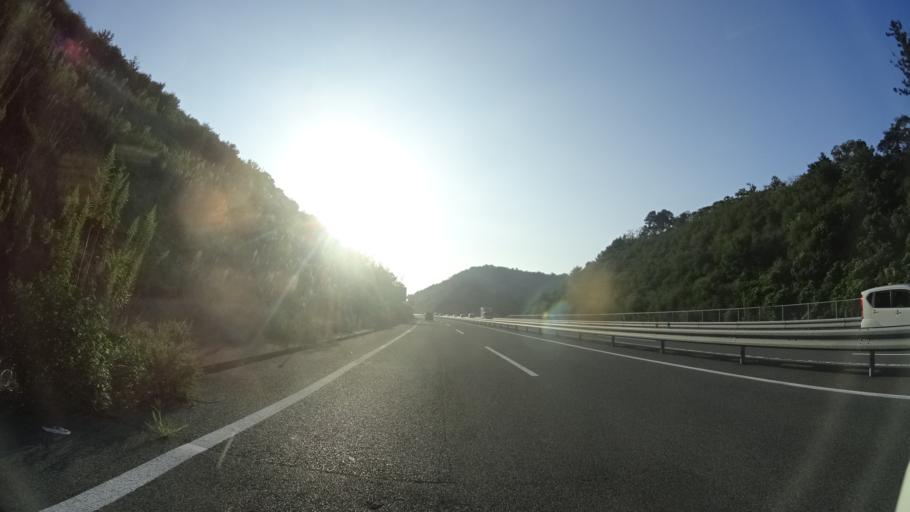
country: JP
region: Yamaguchi
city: Hagi
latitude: 34.3888
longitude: 131.3330
